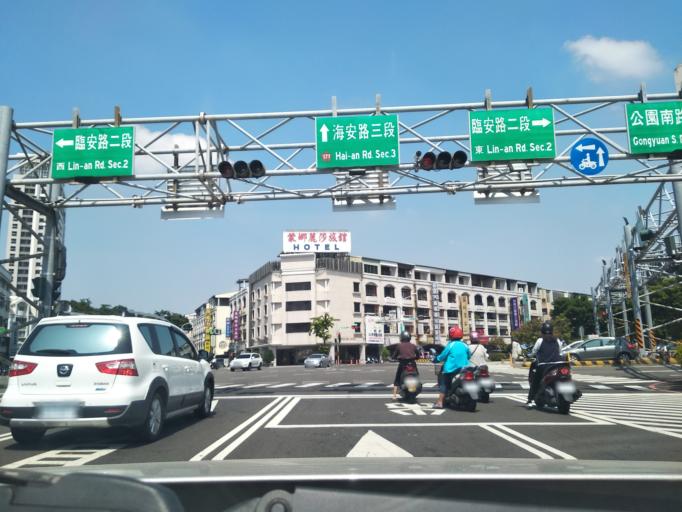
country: TW
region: Taiwan
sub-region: Tainan
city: Tainan
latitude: 23.0035
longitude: 120.2000
